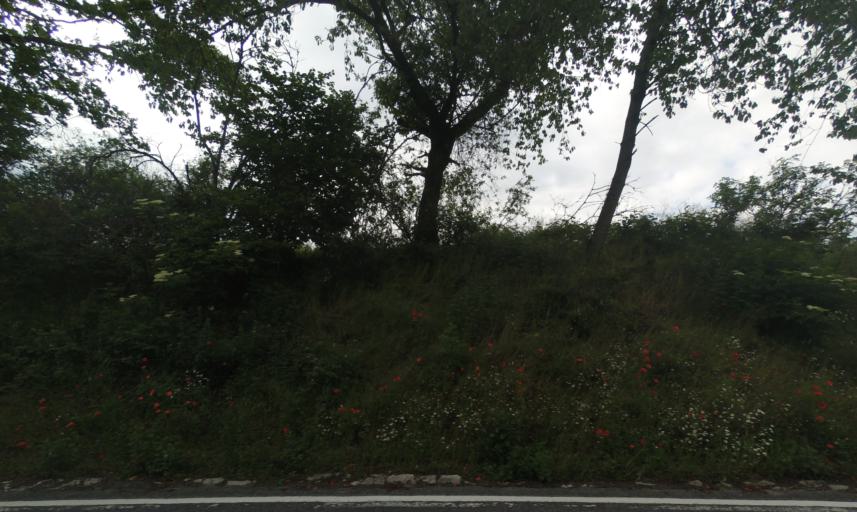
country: DE
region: Bavaria
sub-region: Upper Franconia
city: Schlusselfeld
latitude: 49.7780
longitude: 10.6474
